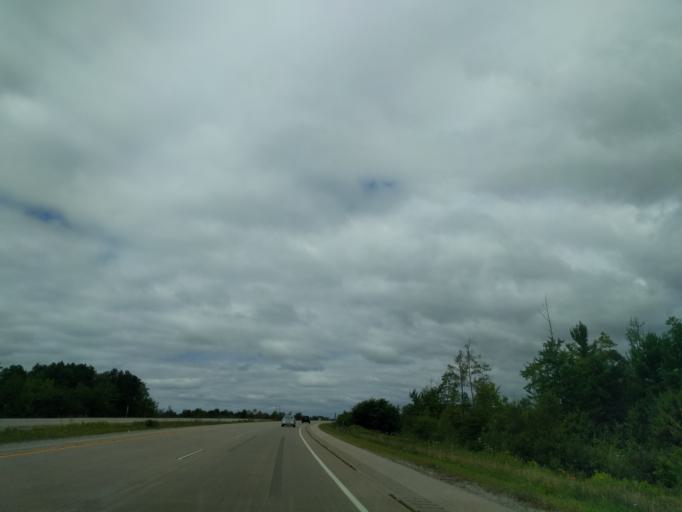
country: US
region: Wisconsin
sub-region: Marinette County
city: Peshtigo
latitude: 45.0404
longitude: -87.7519
